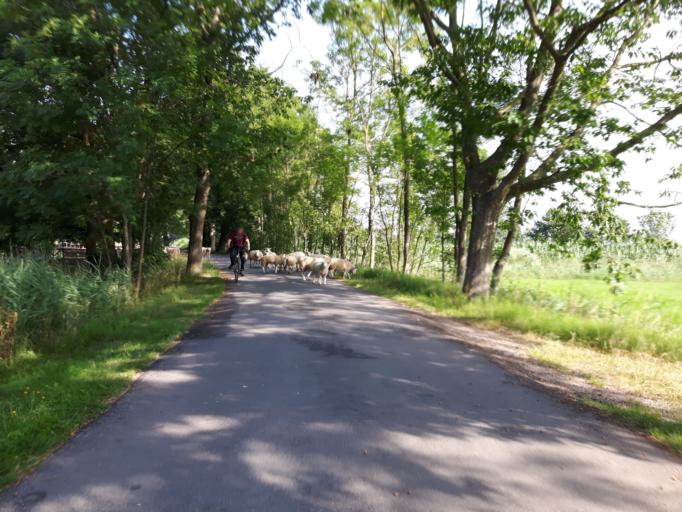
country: DE
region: Lower Saxony
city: Neuenkirchen
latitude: 53.1640
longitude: 8.5128
